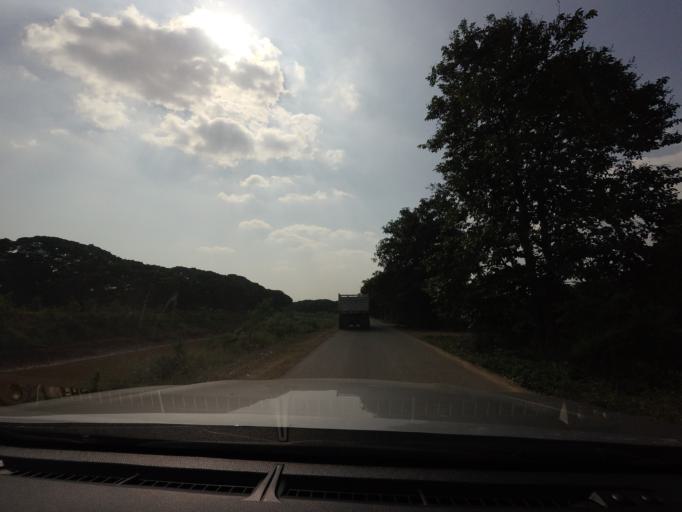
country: TH
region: Phitsanulok
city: Phitsanulok
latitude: 16.8059
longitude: 100.2153
